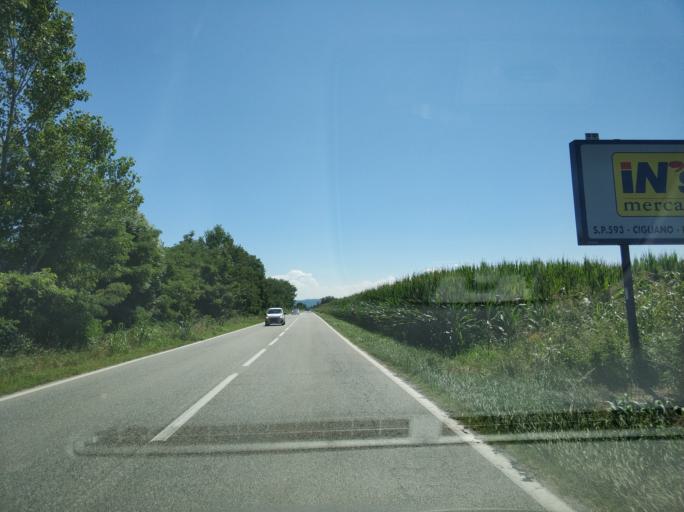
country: IT
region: Piedmont
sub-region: Provincia di Torino
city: Villareggia
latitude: 45.2833
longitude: 7.9902
